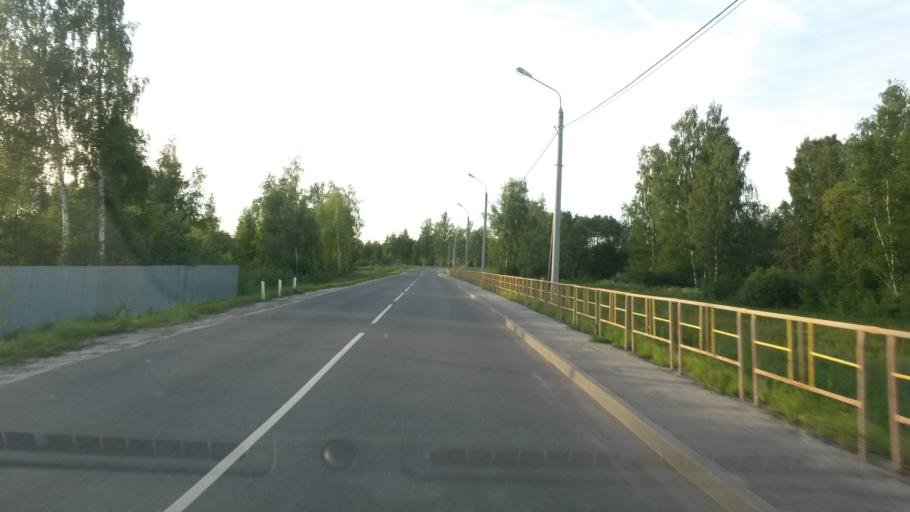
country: RU
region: Jaroslavl
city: Yaroslavl
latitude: 57.7016
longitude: 39.8306
